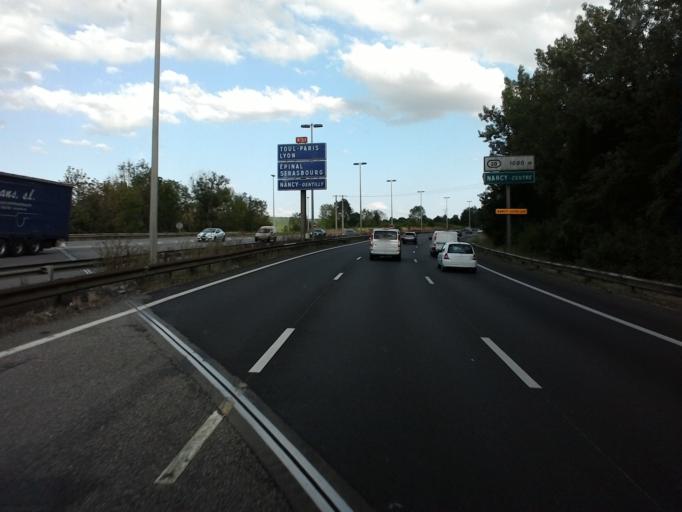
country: FR
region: Lorraine
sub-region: Departement de Meurthe-et-Moselle
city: Champigneulles
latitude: 48.7280
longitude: 6.1660
